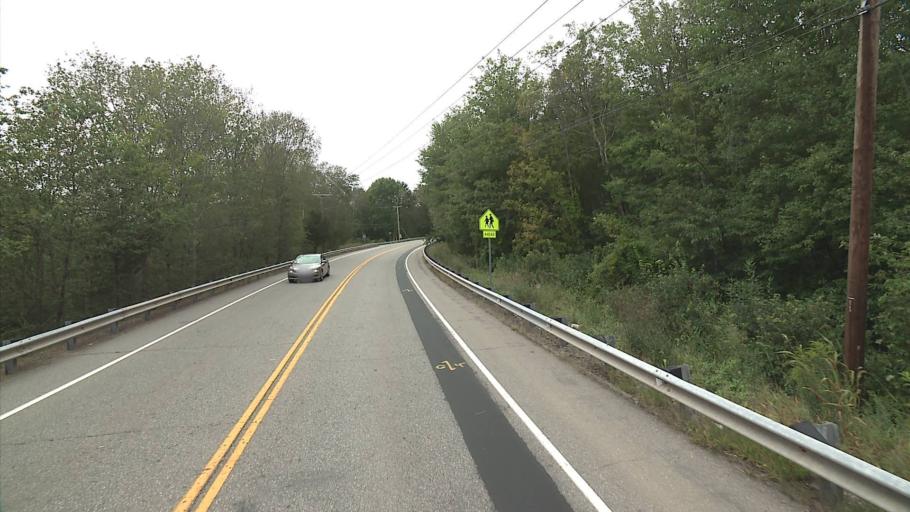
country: US
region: Connecticut
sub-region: Tolland County
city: Hebron
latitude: 41.6745
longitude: -72.4056
